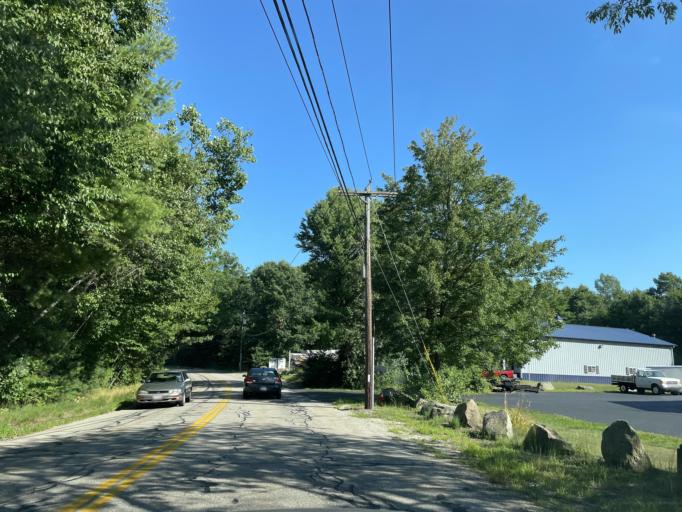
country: US
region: Massachusetts
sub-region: Worcester County
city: East Douglas
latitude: 42.0592
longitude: -71.6886
